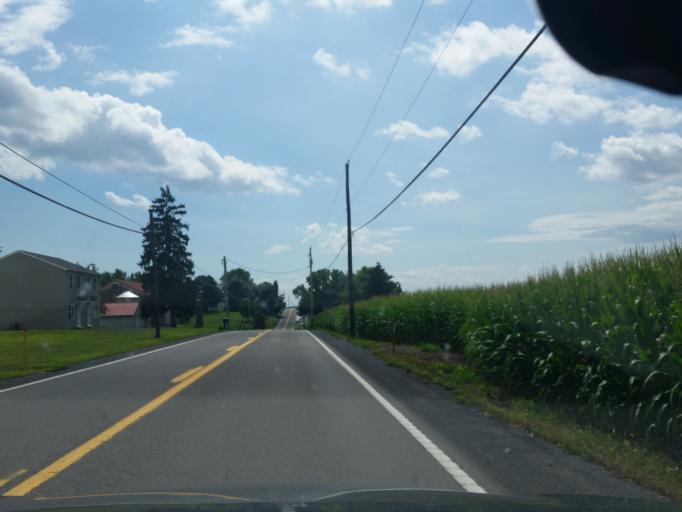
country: US
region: Pennsylvania
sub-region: Dauphin County
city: Elizabethville
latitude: 40.5193
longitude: -76.8422
